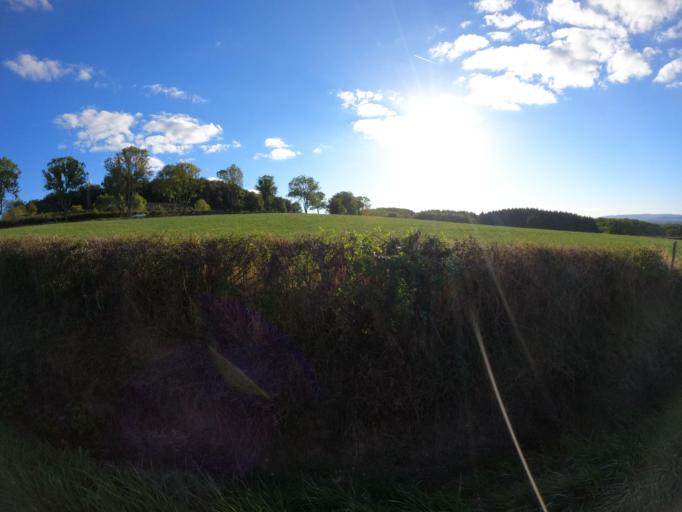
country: FR
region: Bourgogne
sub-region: Departement de Saone-et-Loire
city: Ecuisses
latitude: 46.7387
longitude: 4.5501
